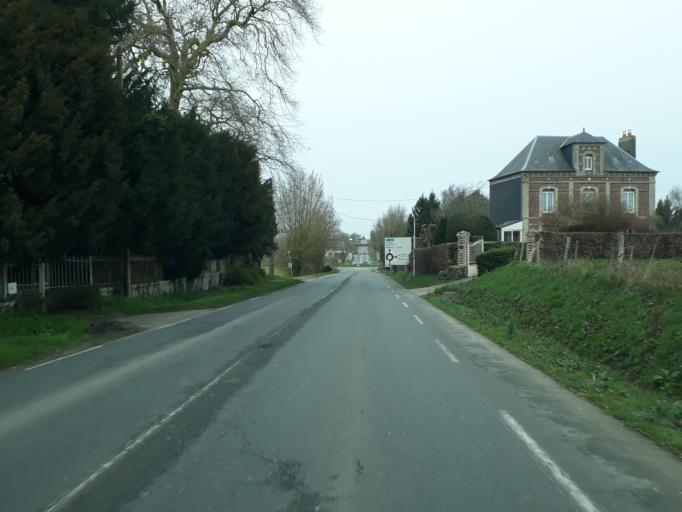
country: FR
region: Haute-Normandie
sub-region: Departement de la Seine-Maritime
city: Beuzeville-la-Grenier
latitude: 49.5994
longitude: 0.4182
